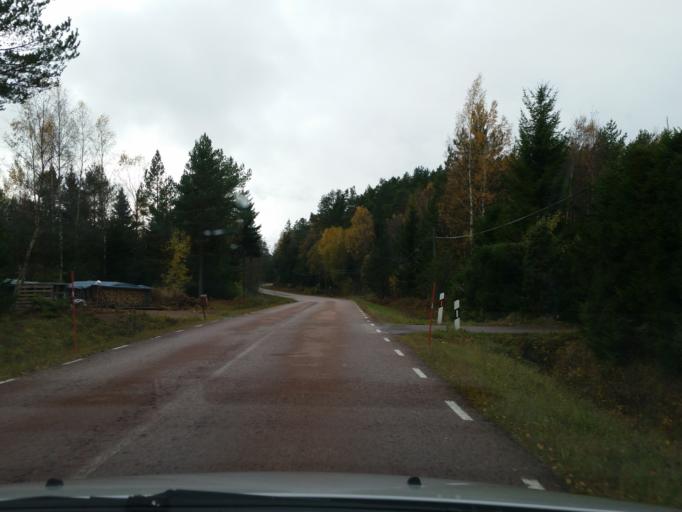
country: AX
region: Alands landsbygd
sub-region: Lemland
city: Lemland
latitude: 60.0206
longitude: 20.1467
